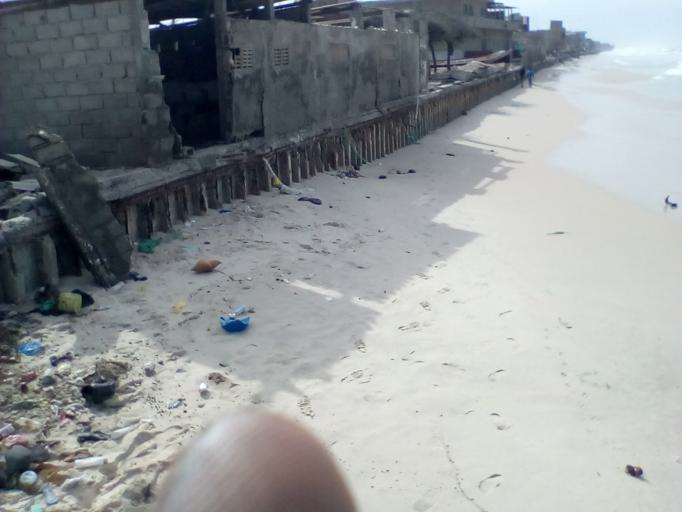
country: SN
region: Saint-Louis
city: Saint-Louis
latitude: 16.0368
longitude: -16.5090
